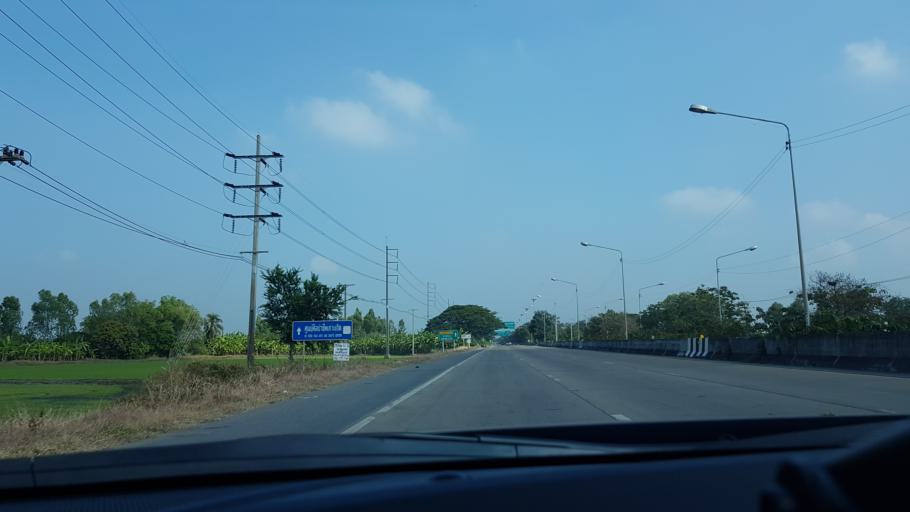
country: TH
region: Phra Nakhon Si Ayutthaya
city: Bang Pa-in
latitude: 14.1431
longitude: 100.5691
